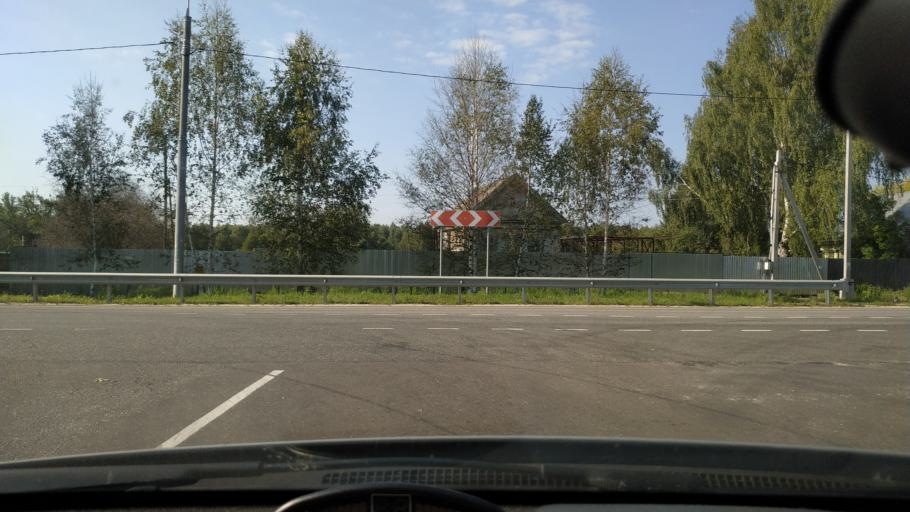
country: RU
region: Moskovskaya
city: Dmitrovskiy Pogost
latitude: 55.2353
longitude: 39.9050
